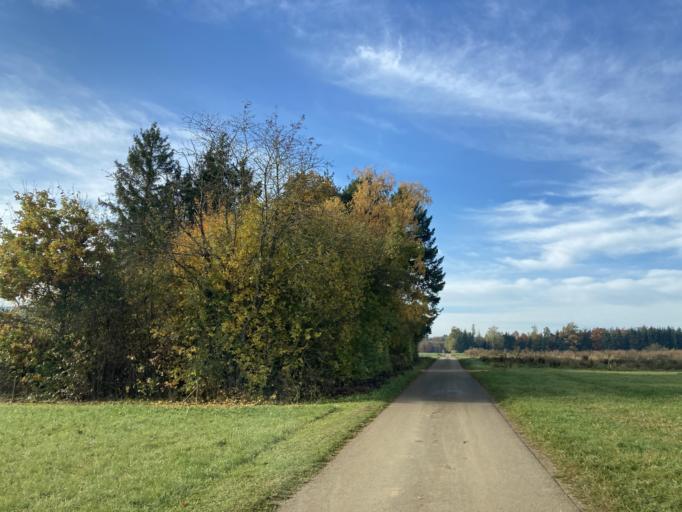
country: DE
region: Baden-Wuerttemberg
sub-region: Tuebingen Region
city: Ofterdingen
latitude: 48.4001
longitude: 9.0099
